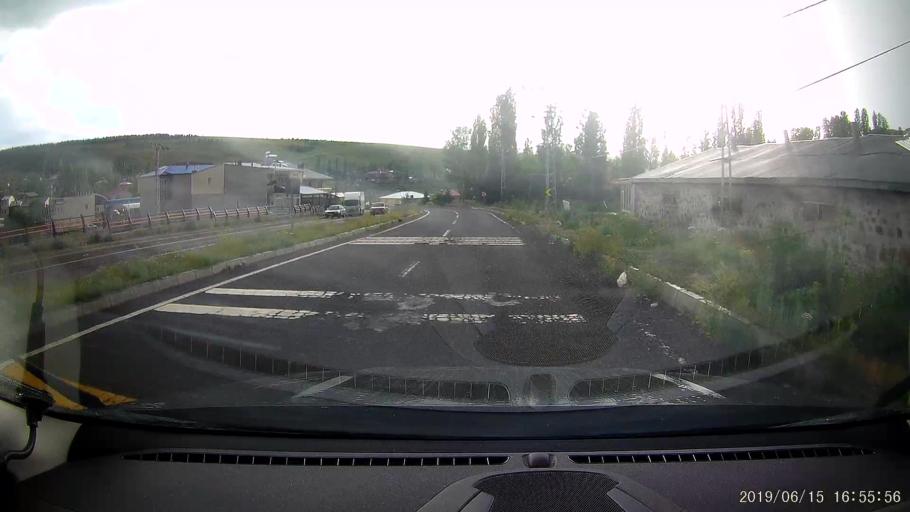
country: TR
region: Kars
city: Susuz
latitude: 40.7825
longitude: 43.1281
